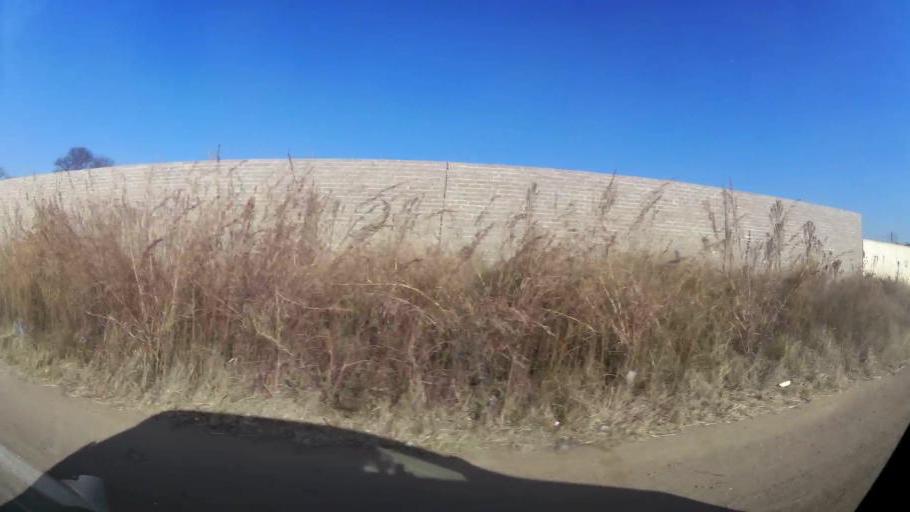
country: ZA
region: Gauteng
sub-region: West Rand District Municipality
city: Muldersdriseloop
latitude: -26.0230
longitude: 27.8747
